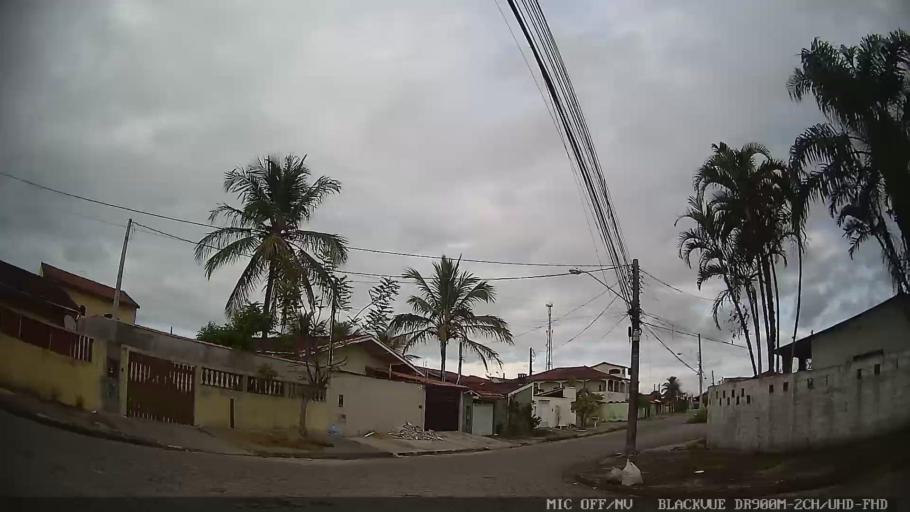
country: BR
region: Sao Paulo
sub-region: Itanhaem
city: Itanhaem
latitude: -24.1918
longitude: -46.8145
